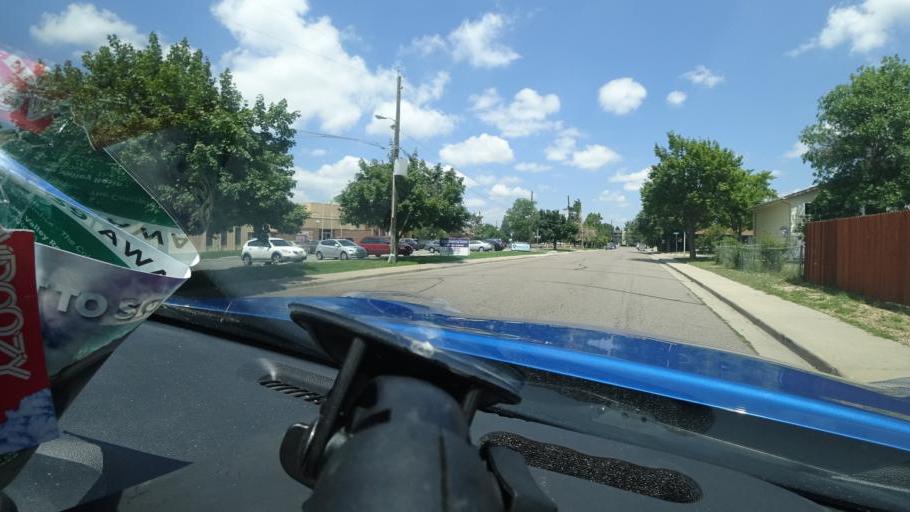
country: US
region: Colorado
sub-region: Adams County
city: Aurora
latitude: 39.7091
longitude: -104.8572
